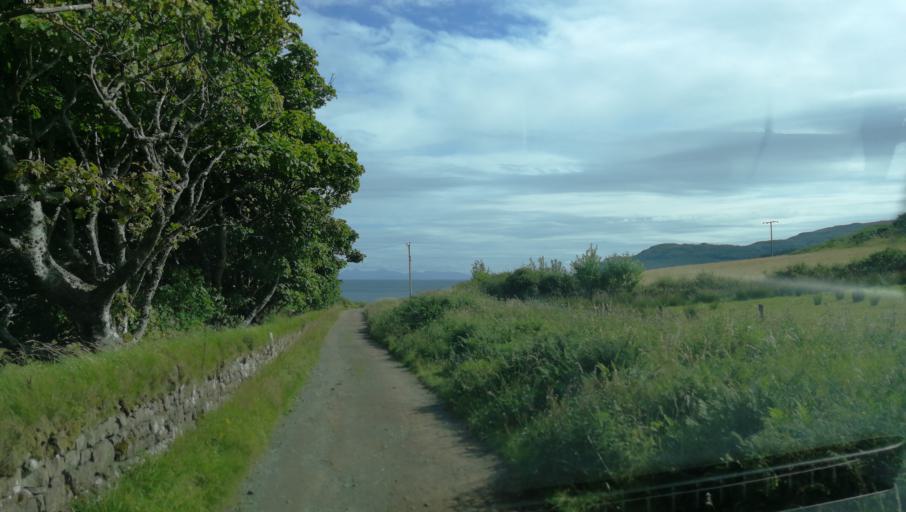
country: GB
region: Scotland
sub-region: Highland
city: Isle of Skye
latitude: 57.3936
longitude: -6.5657
